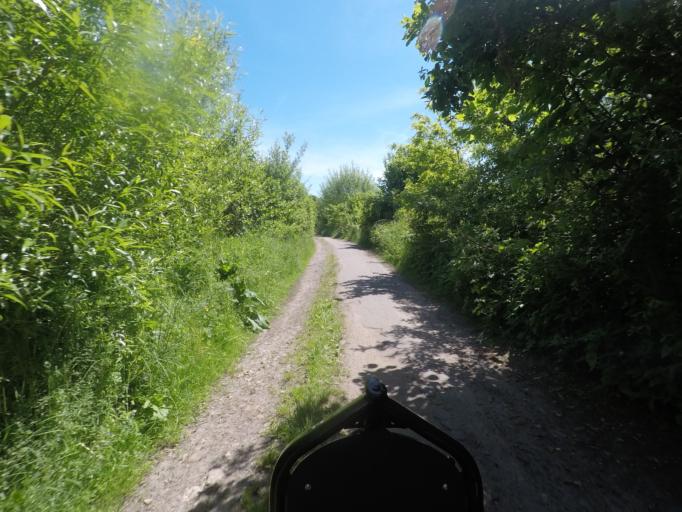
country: DE
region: Schleswig-Holstein
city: Stapelfeld
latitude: 53.6352
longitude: 10.1982
